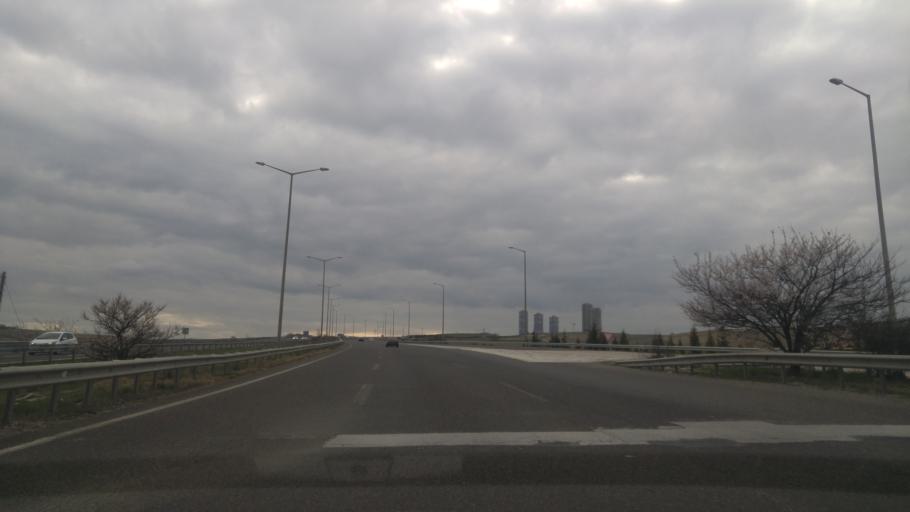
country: TR
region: Ankara
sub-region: Goelbasi
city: Golbasi
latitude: 39.7873
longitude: 32.7251
